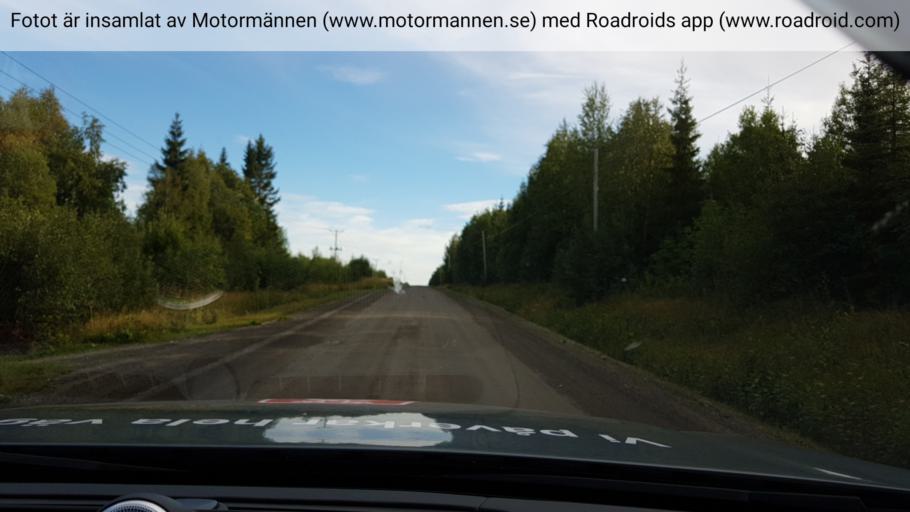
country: SE
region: Jaemtland
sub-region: Stroemsunds Kommun
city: Stroemsund
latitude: 63.9984
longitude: 15.8176
